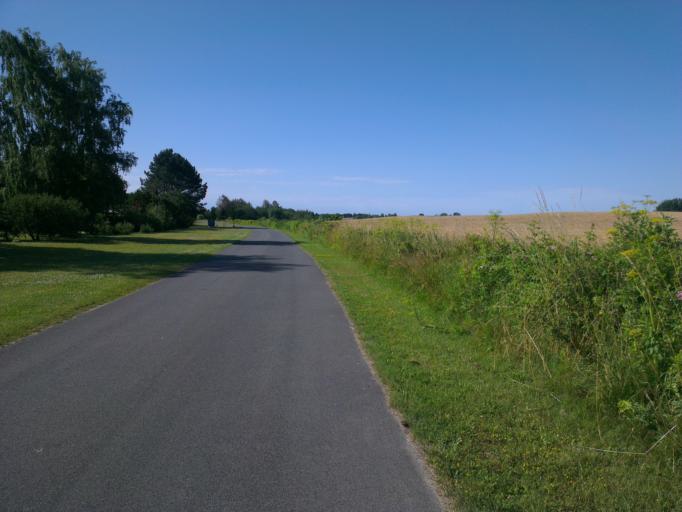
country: DK
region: Zealand
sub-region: Roskilde Kommune
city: Jyllinge
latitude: 55.7775
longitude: 12.0519
